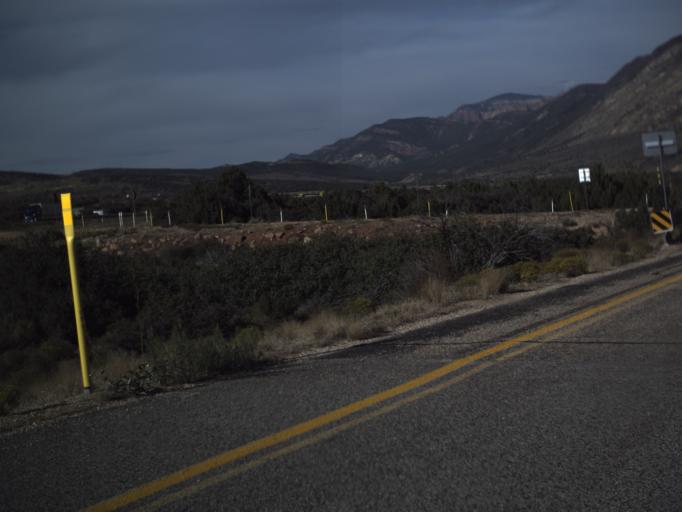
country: US
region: Utah
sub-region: Washington County
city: Toquerville
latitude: 37.3212
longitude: -113.2880
